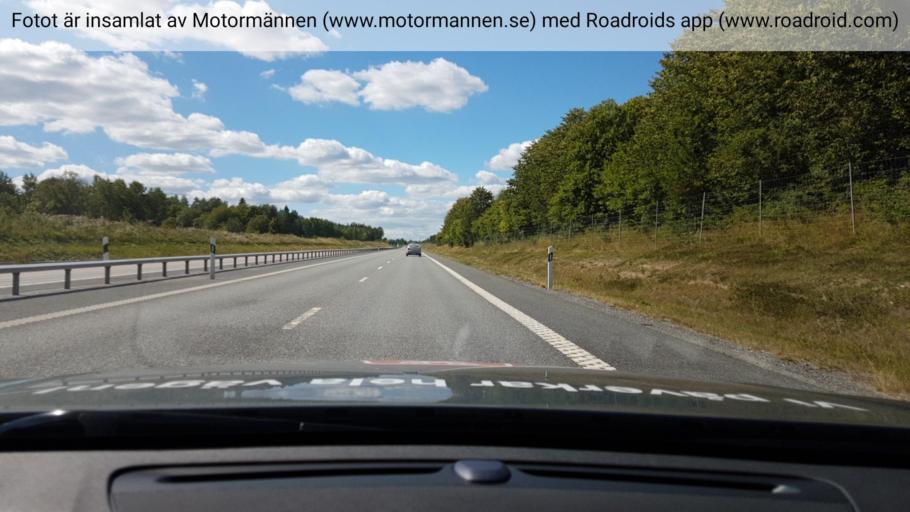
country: SE
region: Stockholm
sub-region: Haninge Kommun
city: Jordbro
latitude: 59.0951
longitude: 18.1049
